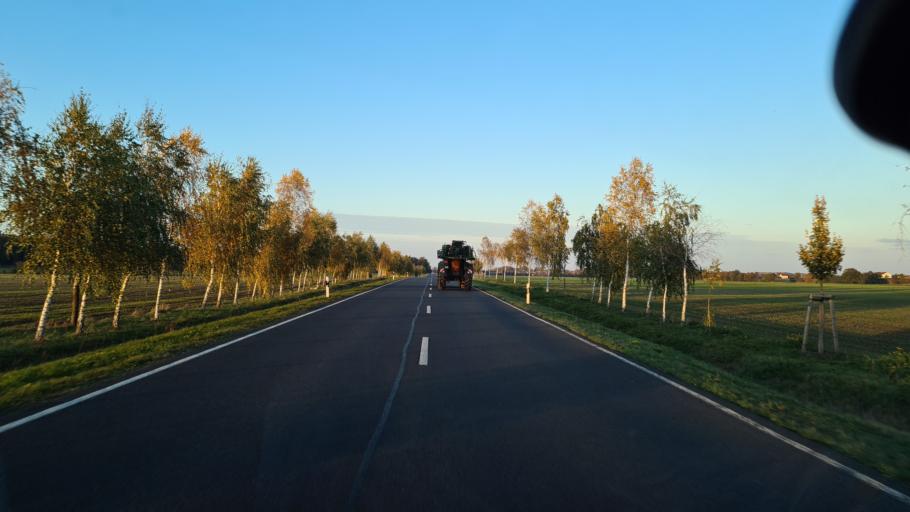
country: DE
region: Saxony
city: Schildau
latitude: 51.4844
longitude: 12.9864
